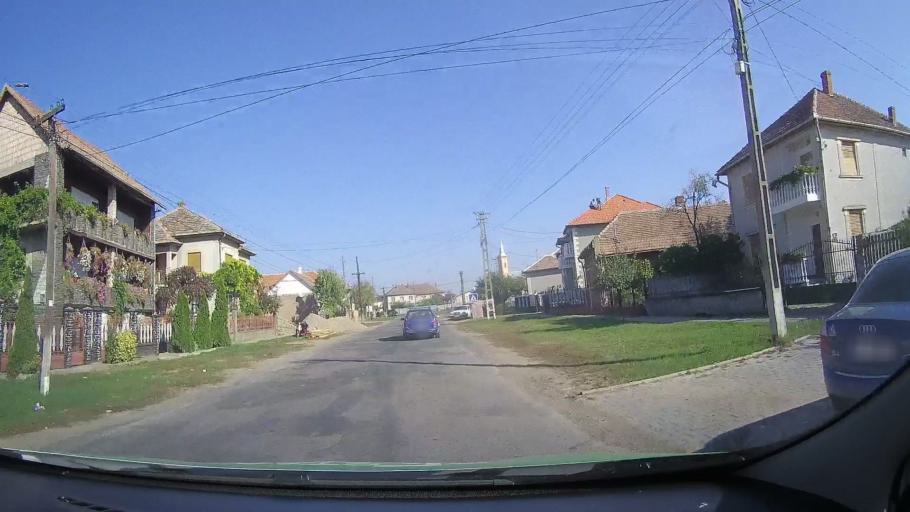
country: RO
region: Satu Mare
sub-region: Comuna Sanislau
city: Sanislau
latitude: 47.6397
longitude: 22.3247
